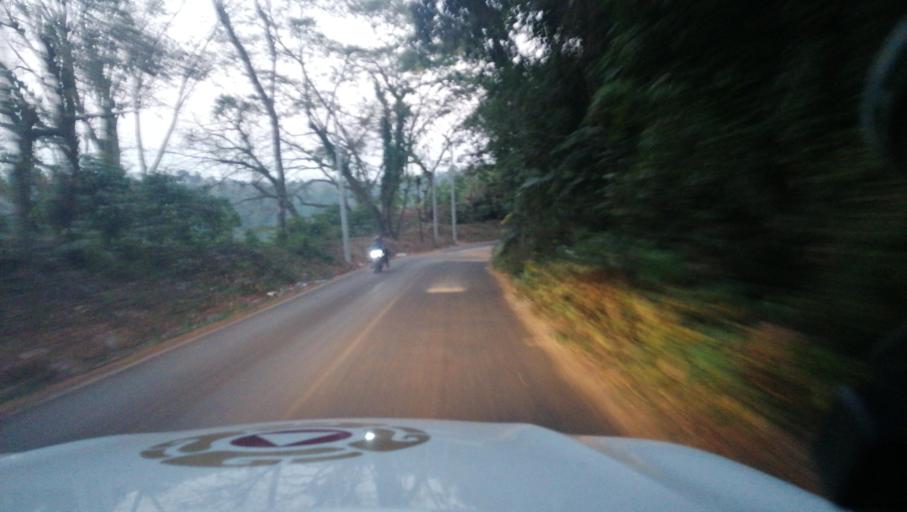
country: MX
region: Chiapas
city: Veinte de Noviembre
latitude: 15.0055
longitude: -92.2447
